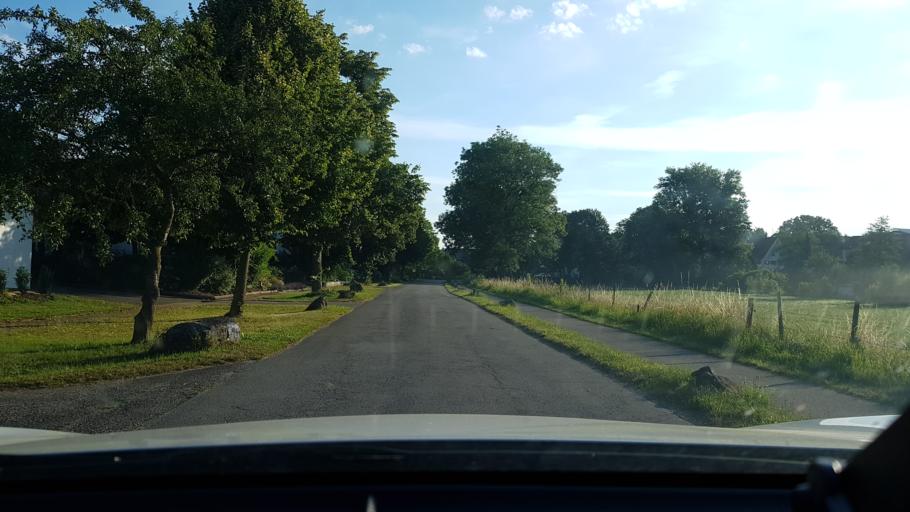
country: DE
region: Baden-Wuerttemberg
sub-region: Tuebingen Region
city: Maselheim
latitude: 48.1680
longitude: 9.8622
